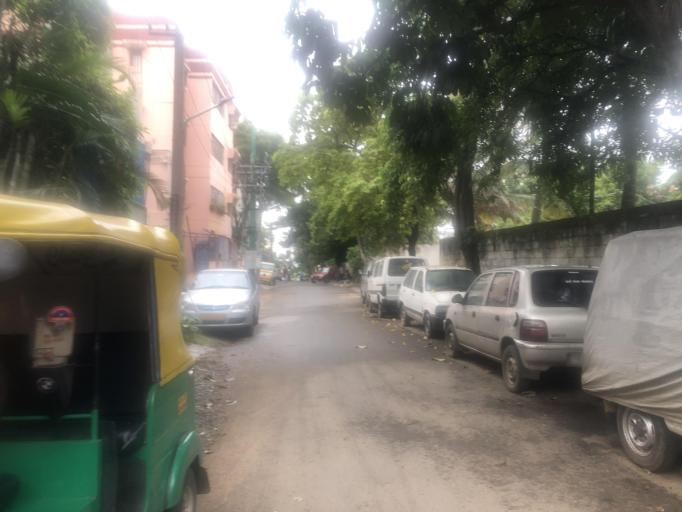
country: IN
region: Karnataka
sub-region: Bangalore Urban
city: Bangalore
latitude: 12.9393
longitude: 77.5385
